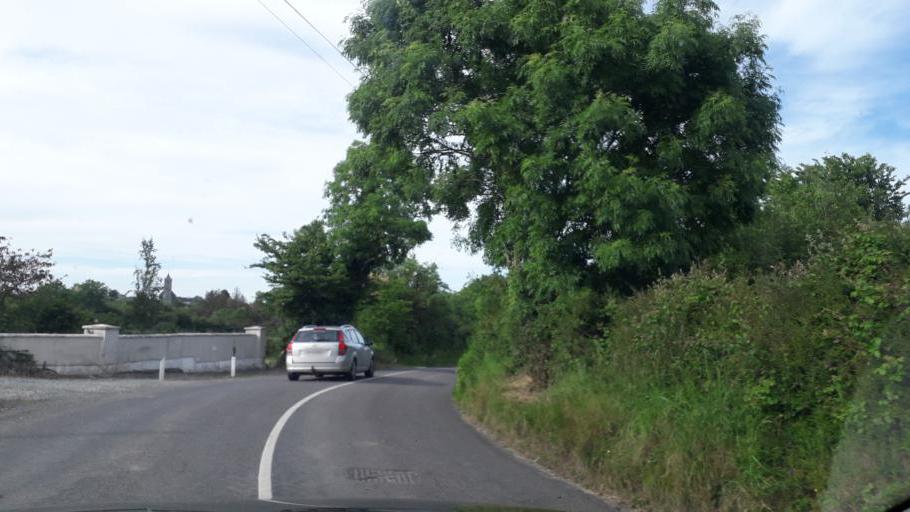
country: IE
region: Leinster
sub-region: Loch Garman
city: Courtown
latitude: 52.5667
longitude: -6.2310
